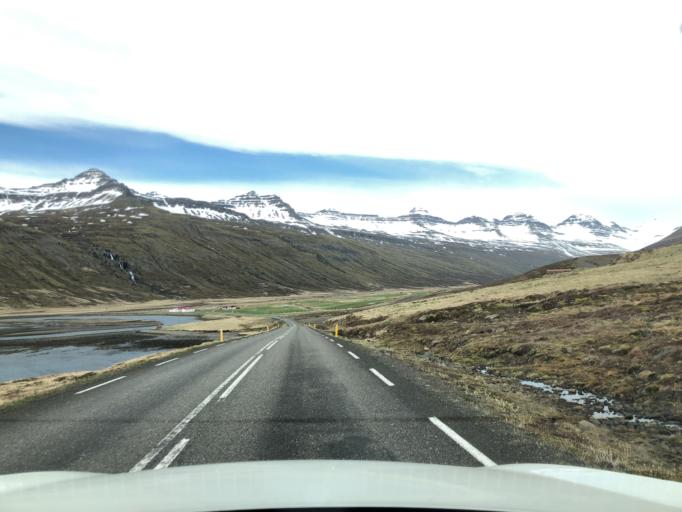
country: IS
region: East
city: Eskifjoerdur
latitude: 64.8414
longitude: -13.9419
